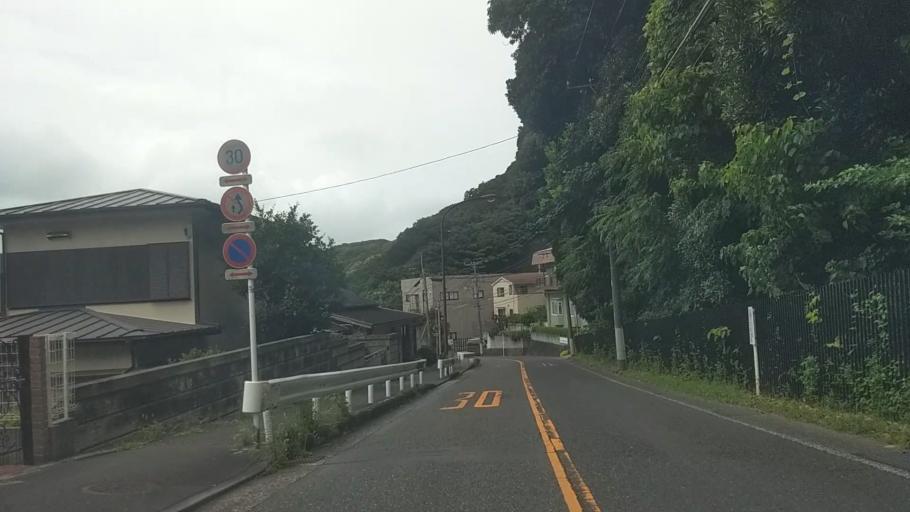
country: JP
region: Kanagawa
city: Yokosuka
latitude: 35.2573
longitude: 139.7192
